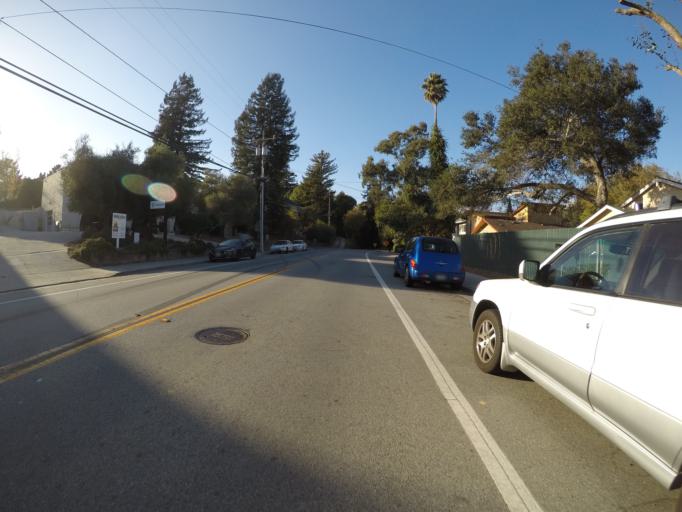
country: US
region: California
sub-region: Santa Cruz County
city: Pasatiempo
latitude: 36.9911
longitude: -122.0324
